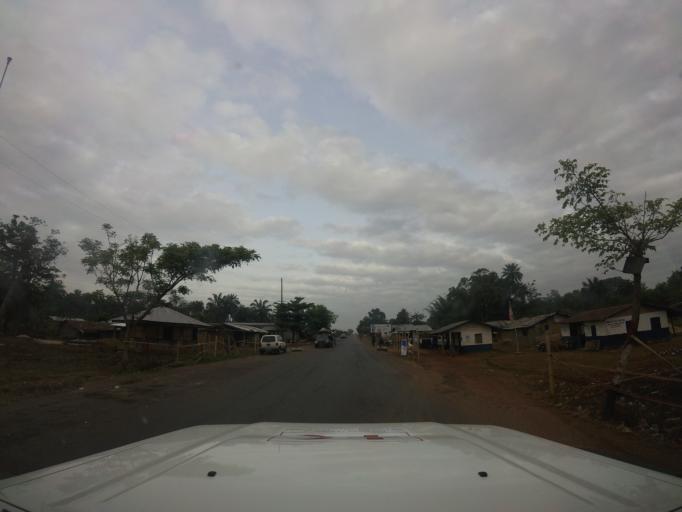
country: LR
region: Bomi
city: Tubmanburg
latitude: 6.7214
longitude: -10.9803
